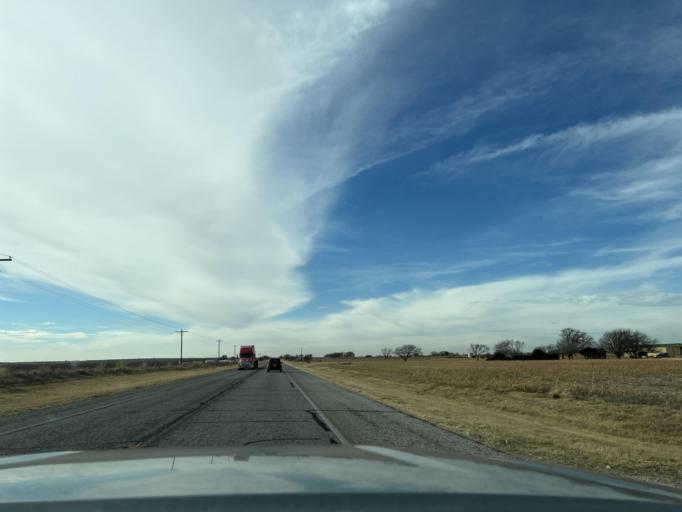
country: US
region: Texas
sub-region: Fisher County
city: Roby
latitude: 32.7572
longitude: -100.2778
